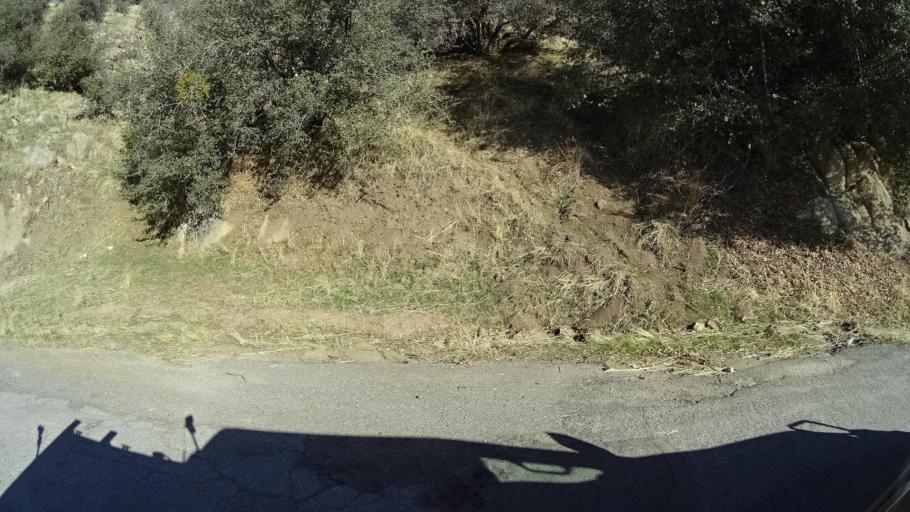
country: US
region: California
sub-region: Kern County
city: Bodfish
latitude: 35.4510
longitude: -118.6581
